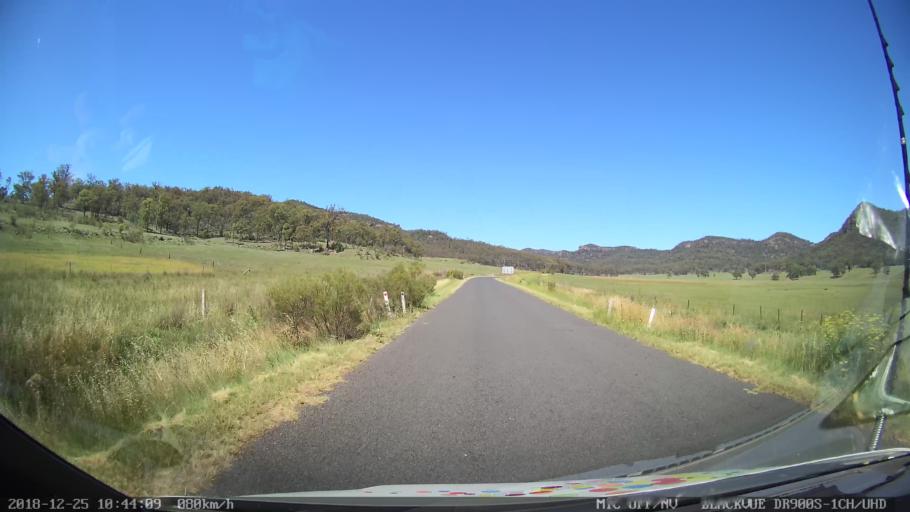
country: AU
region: New South Wales
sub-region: Upper Hunter Shire
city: Merriwa
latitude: -32.4267
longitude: 150.3042
